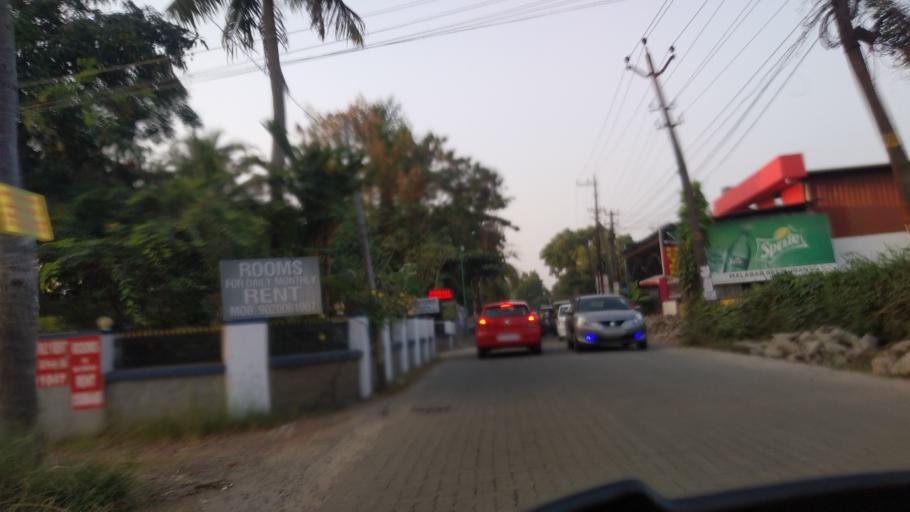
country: IN
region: Kerala
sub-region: Ernakulam
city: Elur
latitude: 10.0433
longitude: 76.2741
